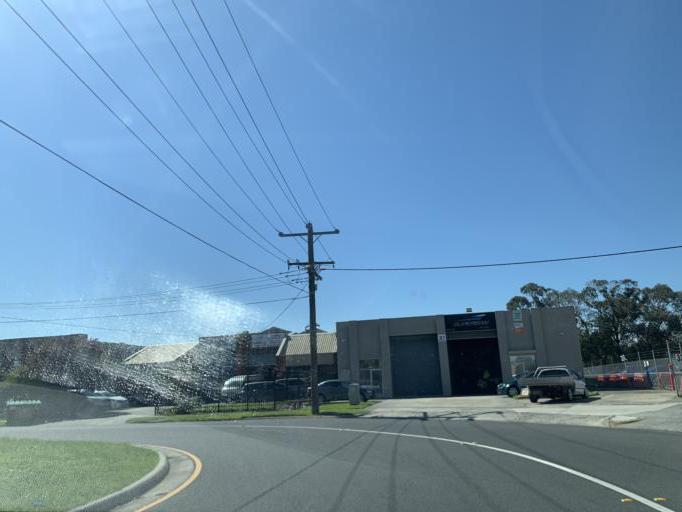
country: AU
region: Victoria
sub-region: Greater Dandenong
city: Dandenong
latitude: -37.9960
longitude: 145.1967
